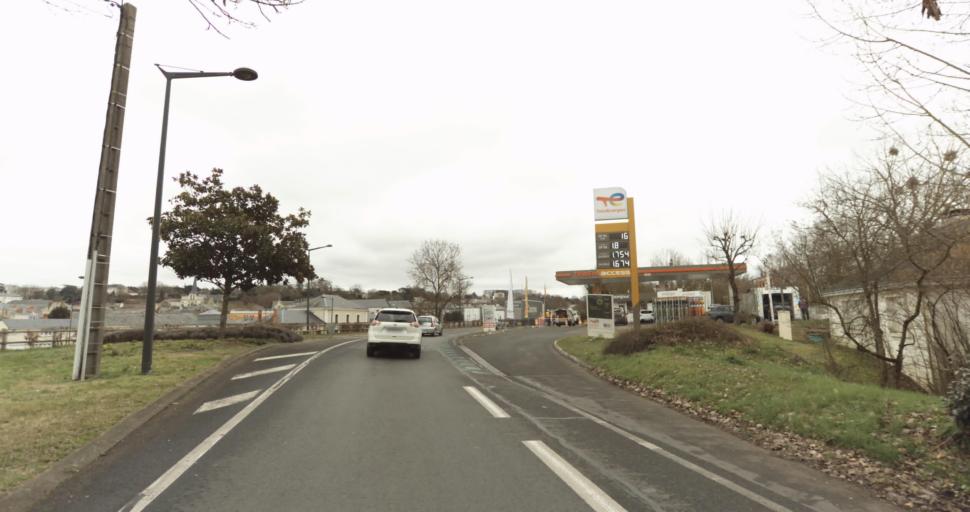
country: FR
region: Pays de la Loire
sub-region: Departement de Maine-et-Loire
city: Saumur
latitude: 47.2521
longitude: -0.0828
